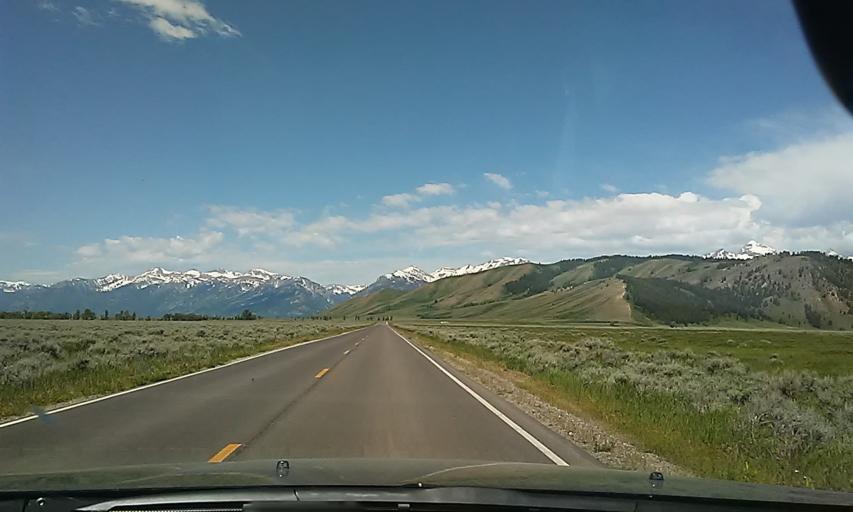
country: US
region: Wyoming
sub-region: Teton County
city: Jackson
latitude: 43.6250
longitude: -110.6455
